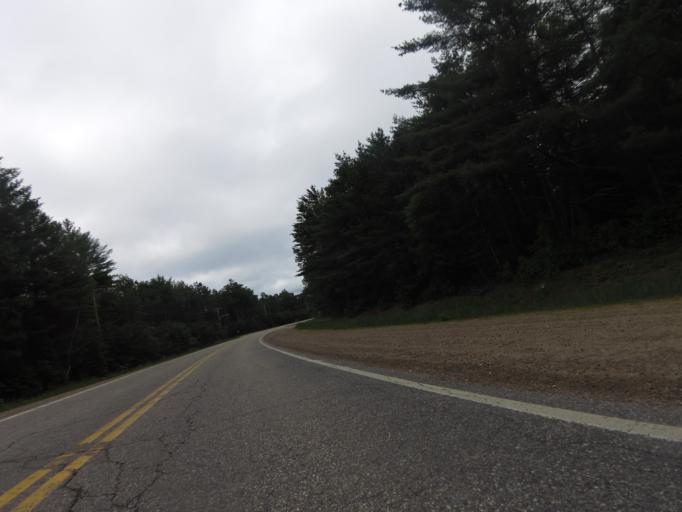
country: CA
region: Quebec
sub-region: Outaouais
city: Shawville
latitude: 45.8590
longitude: -76.4112
